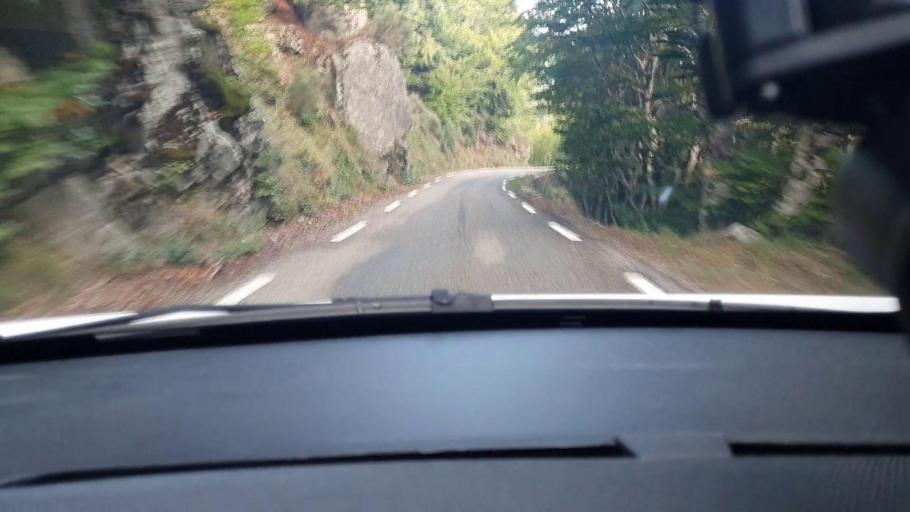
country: FR
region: Languedoc-Roussillon
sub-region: Departement du Gard
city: Branoux-les-Taillades
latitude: 44.3634
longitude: 3.9182
